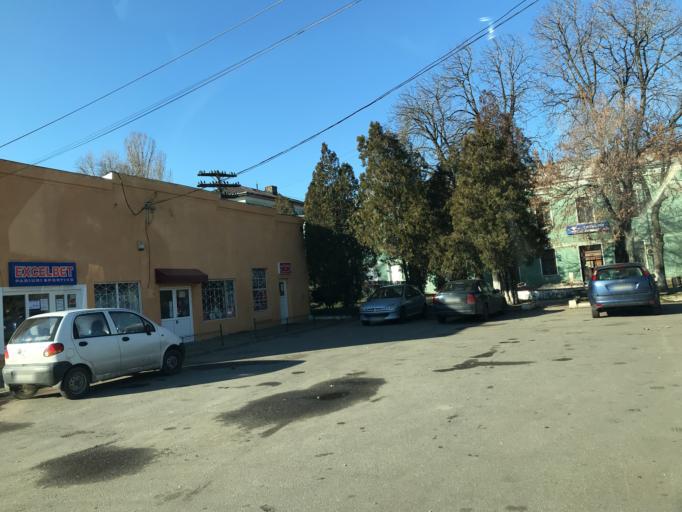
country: RO
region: Olt
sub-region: Comuna Piatra Olt
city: Piatra Olt
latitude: 44.3677
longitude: 24.2557
